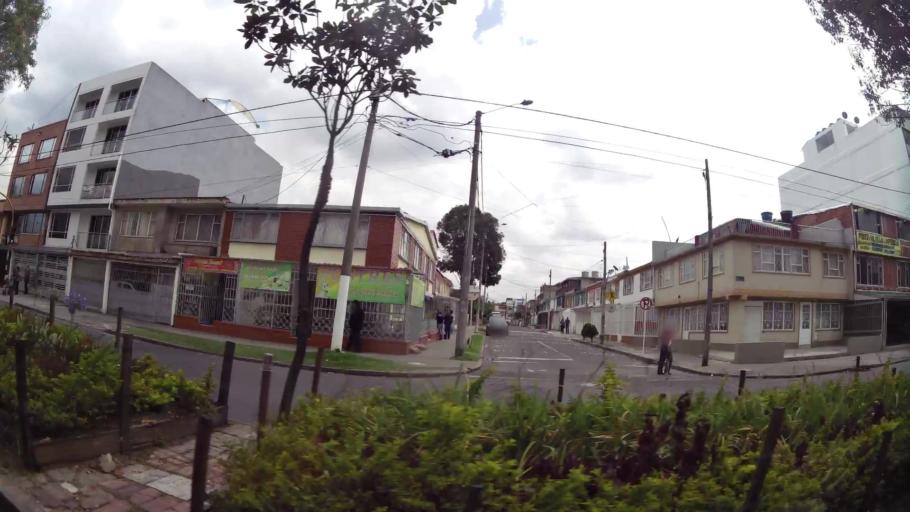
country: CO
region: Bogota D.C.
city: Bogota
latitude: 4.6004
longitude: -74.0965
